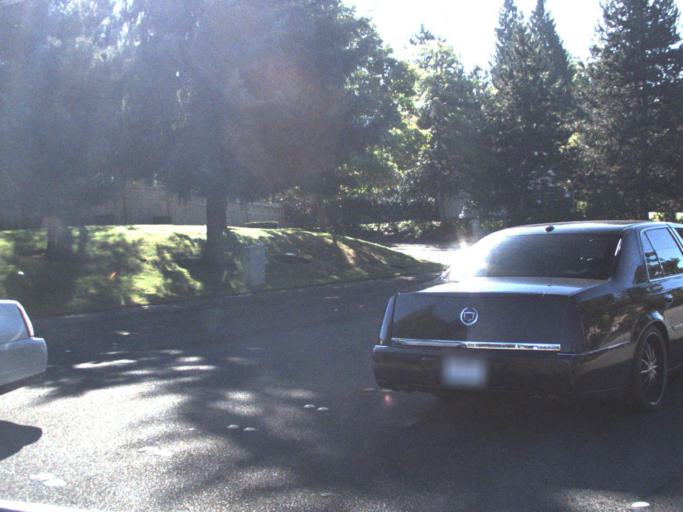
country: US
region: Washington
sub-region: King County
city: Kent
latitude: 47.3792
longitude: -122.2023
